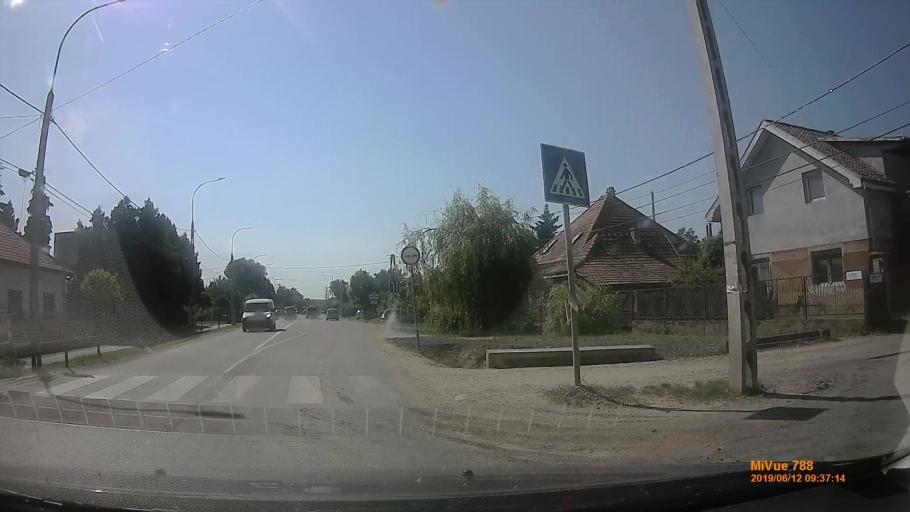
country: HU
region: Pest
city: Gyal
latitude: 47.3766
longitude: 19.2216
